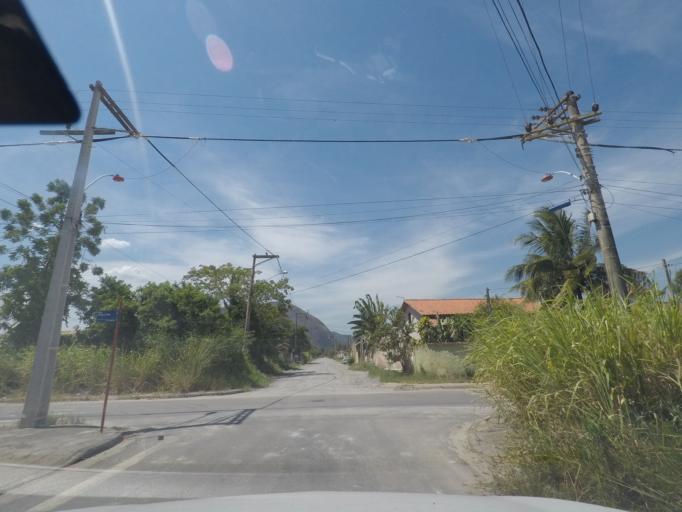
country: BR
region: Rio de Janeiro
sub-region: Marica
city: Marica
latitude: -22.9597
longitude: -42.9586
